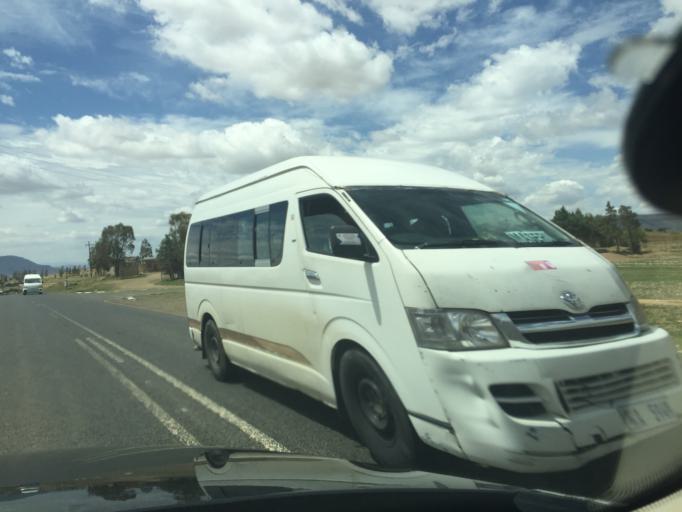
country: LS
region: Mafeteng
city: Mafeteng
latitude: -29.9802
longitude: 27.3228
